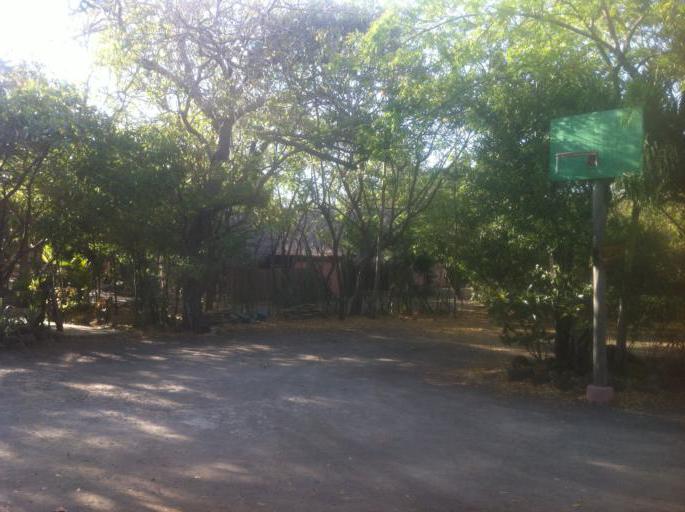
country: NI
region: Managua
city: Carlos Fonseca Amador
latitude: 11.9157
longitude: -86.6015
